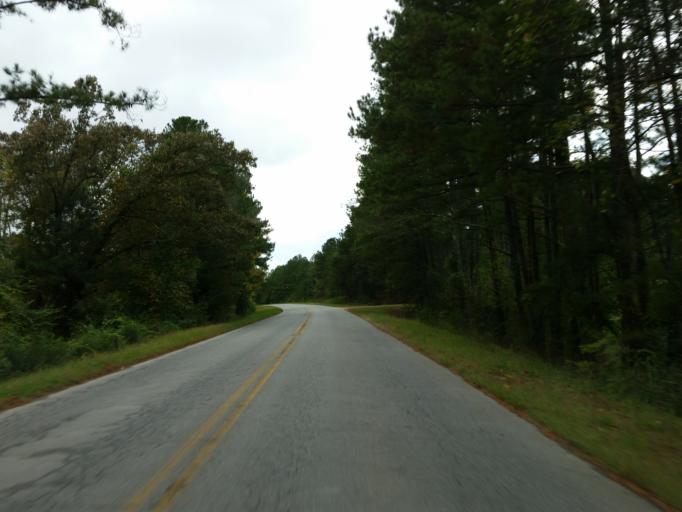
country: US
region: Georgia
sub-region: Bartow County
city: Cartersville
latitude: 34.1159
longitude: -84.8405
